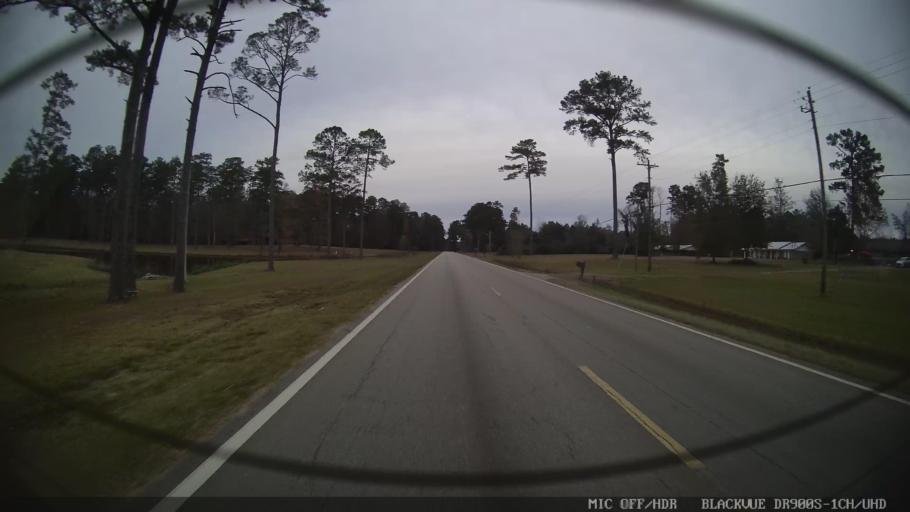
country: US
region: Mississippi
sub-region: Clarke County
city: Stonewall
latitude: 32.0448
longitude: -88.8909
